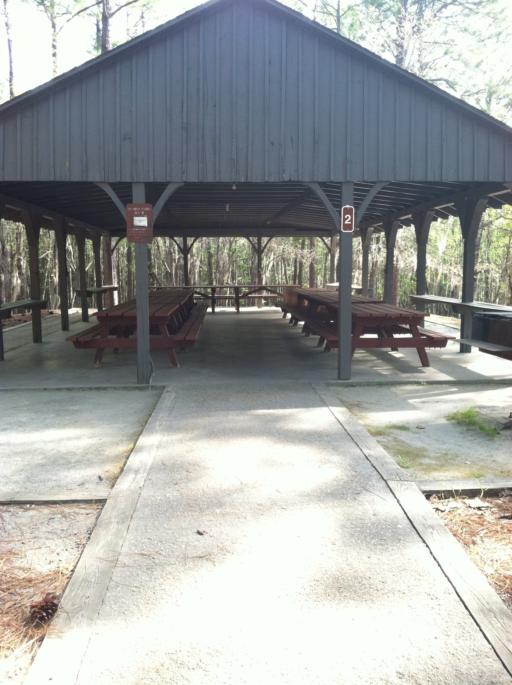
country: US
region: Georgia
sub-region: Emanuel County
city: Twin City
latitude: 32.5522
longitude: -82.1241
